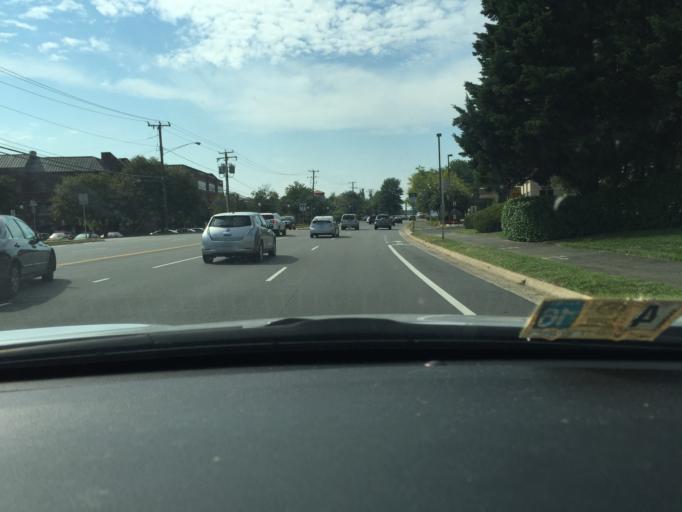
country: US
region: Virginia
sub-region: Fairfax County
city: Tysons Corner
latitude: 38.9110
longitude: -77.2251
